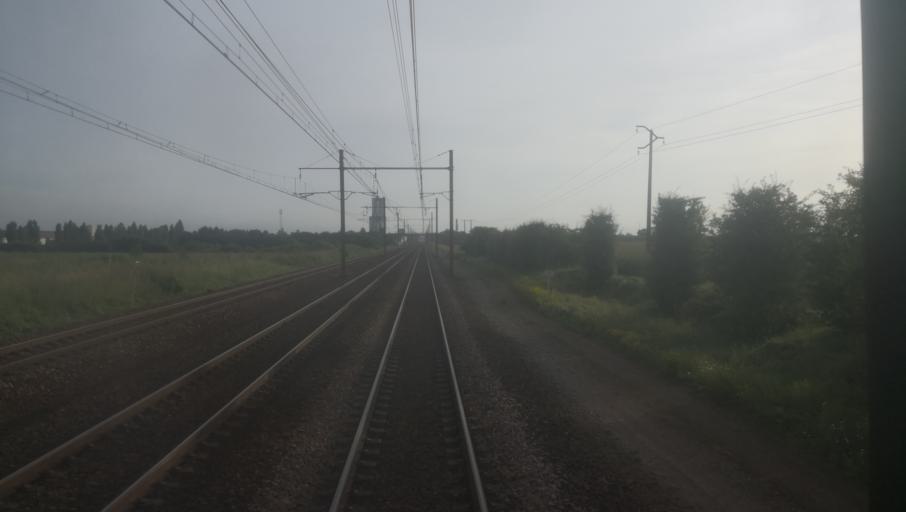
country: FR
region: Centre
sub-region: Departement d'Eure-et-Loir
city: Toury
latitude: 48.1793
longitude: 1.9324
